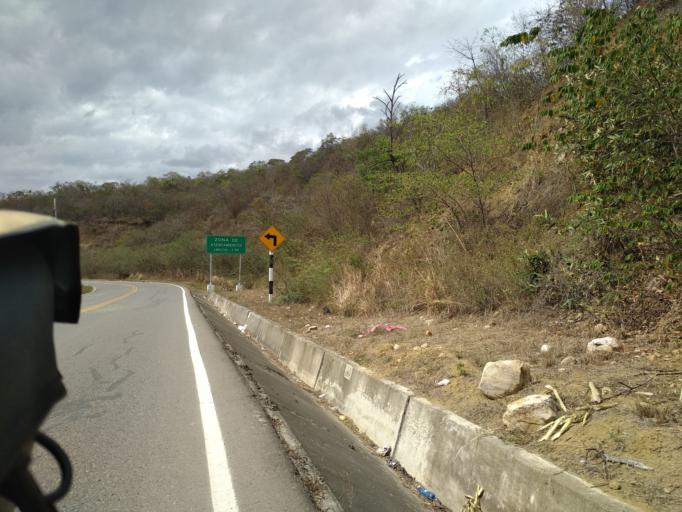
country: PE
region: Amazonas
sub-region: Utcubamba
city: Jamalca
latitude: -5.8383
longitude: -78.2400
